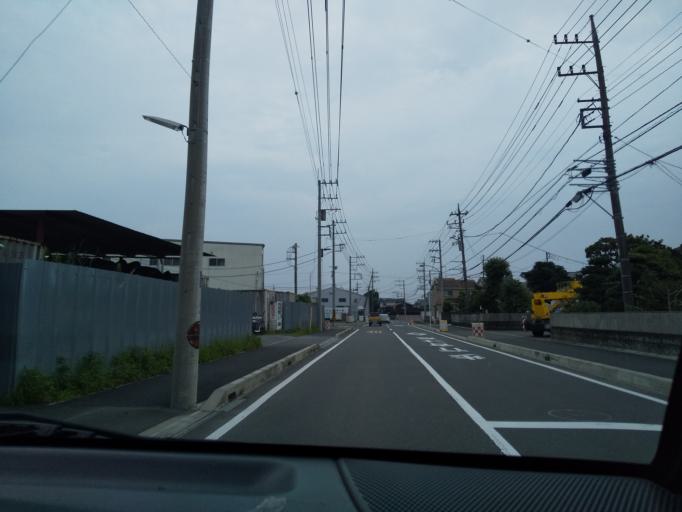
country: JP
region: Kanagawa
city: Atsugi
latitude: 35.4099
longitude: 139.3899
